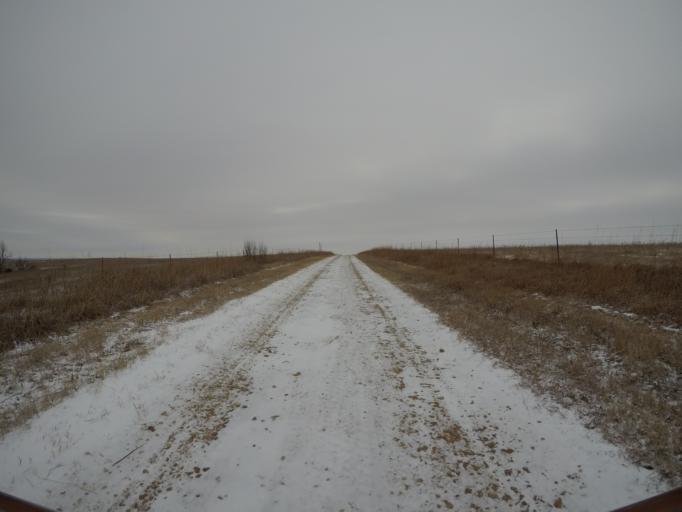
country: US
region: Kansas
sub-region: Wabaunsee County
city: Alma
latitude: 38.8928
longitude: -96.1136
